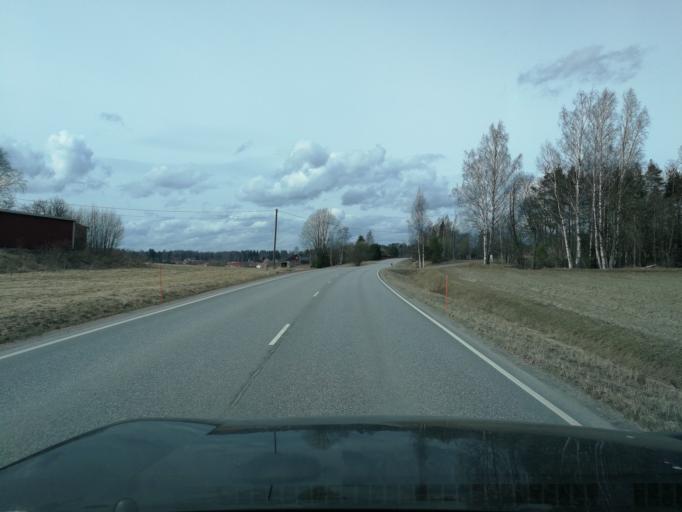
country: FI
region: Uusimaa
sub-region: Helsinki
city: Siuntio
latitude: 60.1230
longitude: 24.2374
